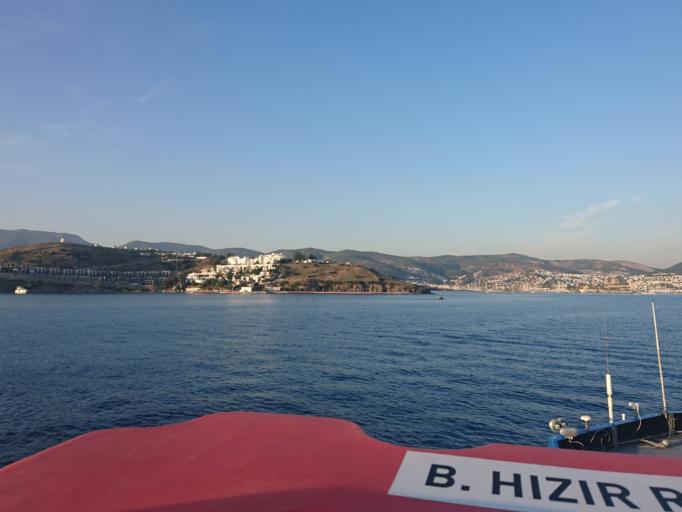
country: TR
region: Mugla
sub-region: Bodrum
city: Bodrum
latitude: 37.0155
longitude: 27.4171
